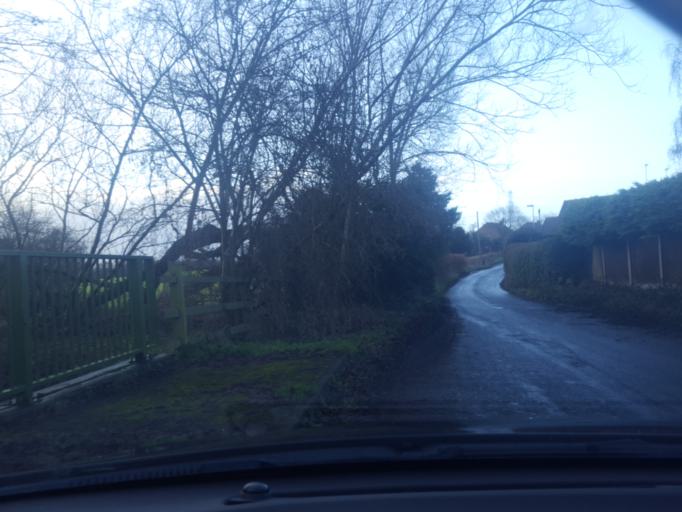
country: GB
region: England
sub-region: Staffordshire
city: Codsall
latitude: 52.6321
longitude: -2.2081
